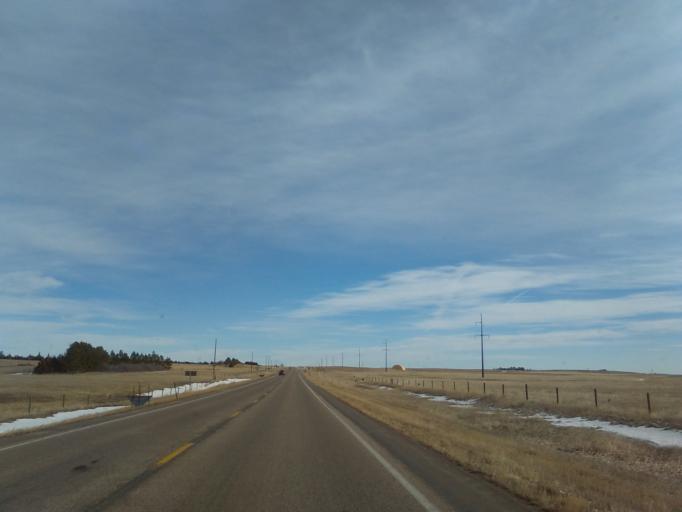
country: US
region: Wyoming
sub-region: Laramie County
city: Pine Bluffs
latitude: 41.4173
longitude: -104.4148
